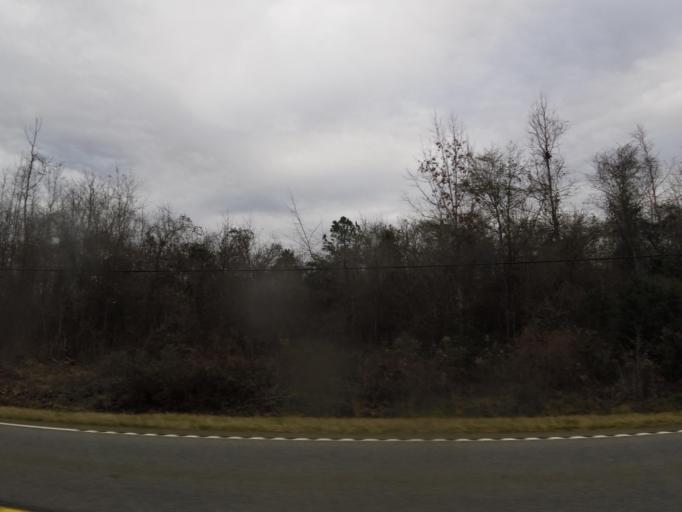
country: US
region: Georgia
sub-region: Randolph County
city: Cuthbert
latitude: 31.7754
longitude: -84.7024
